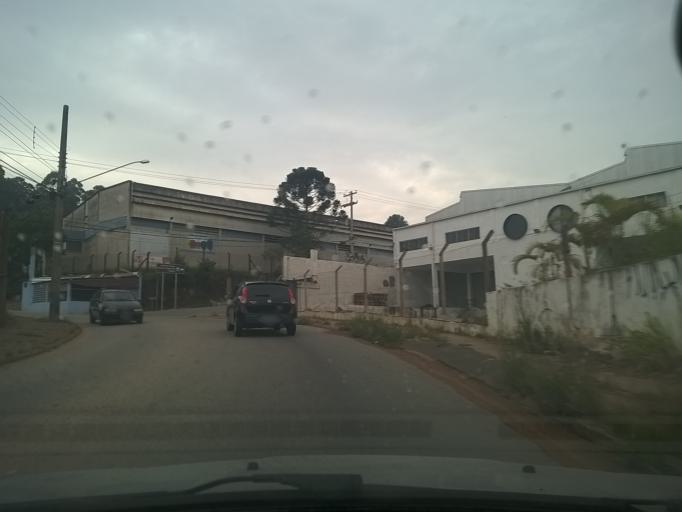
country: BR
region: Sao Paulo
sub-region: Caieiras
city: Caieiras
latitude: -23.3844
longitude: -46.7424
